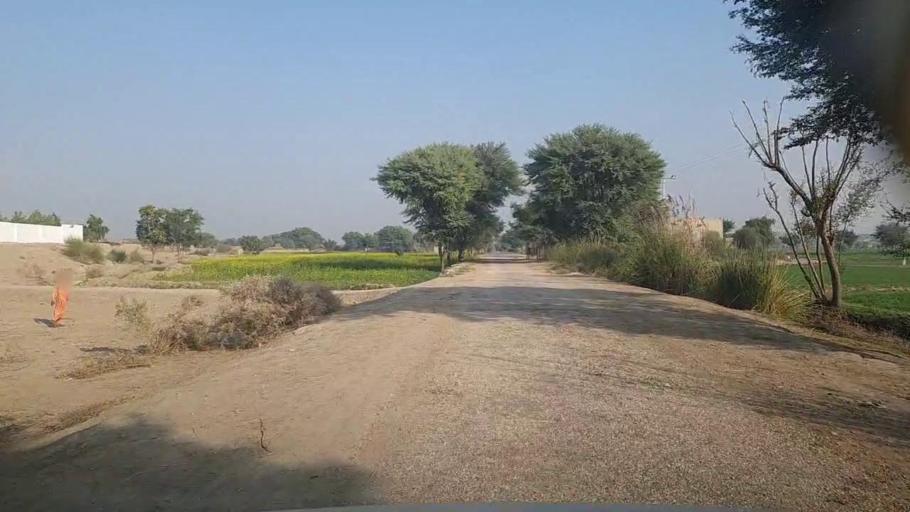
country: PK
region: Sindh
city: Kandiari
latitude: 26.7658
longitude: 68.4964
